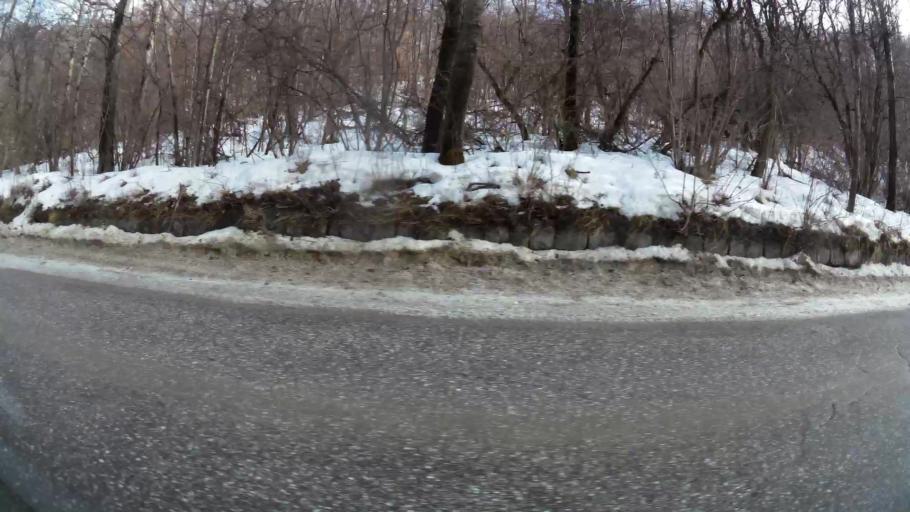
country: BG
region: Sofia-Capital
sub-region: Stolichna Obshtina
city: Sofia
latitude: 42.6313
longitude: 23.2300
